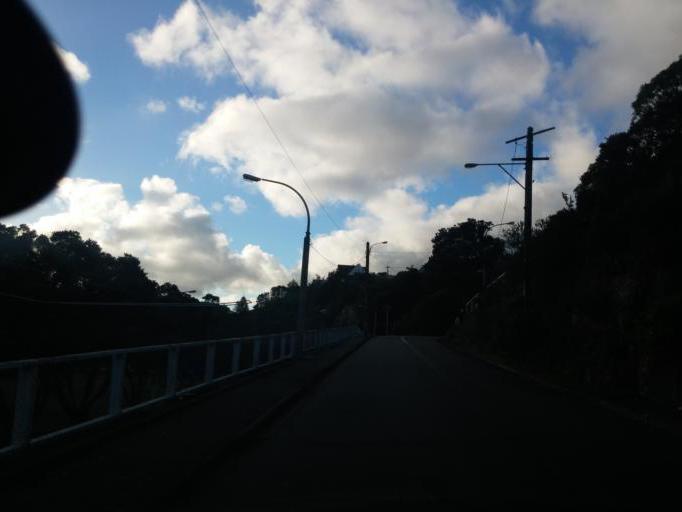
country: NZ
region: Wellington
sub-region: Wellington City
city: Kelburn
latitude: -41.2864
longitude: 174.7548
